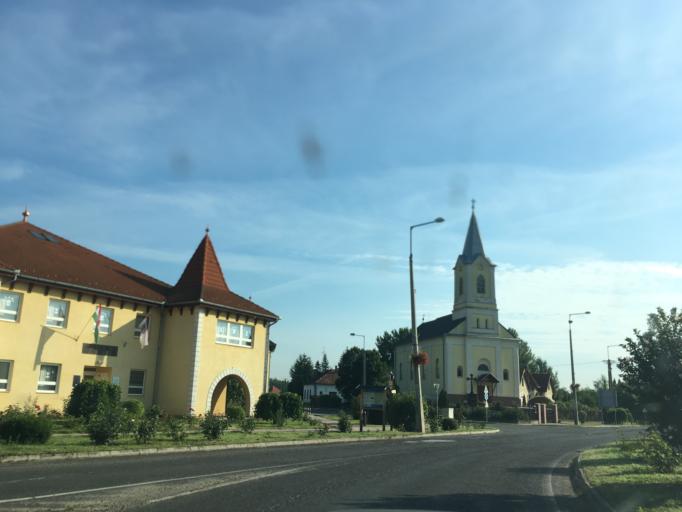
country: HU
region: Szabolcs-Szatmar-Bereg
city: Nyirlugos
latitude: 47.6930
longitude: 22.0450
